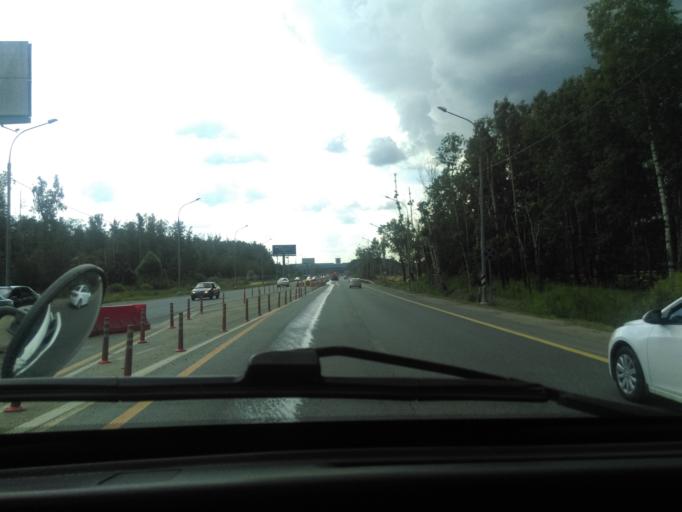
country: RU
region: Moskovskaya
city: Yakovlevskoye
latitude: 55.4238
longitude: 37.8887
